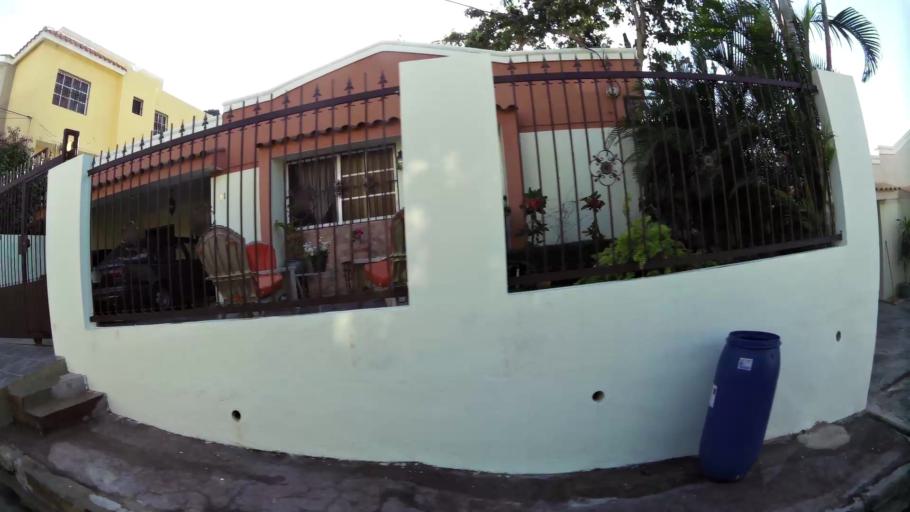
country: DO
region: Nacional
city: Santo Domingo
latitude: 18.4971
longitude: -69.9682
